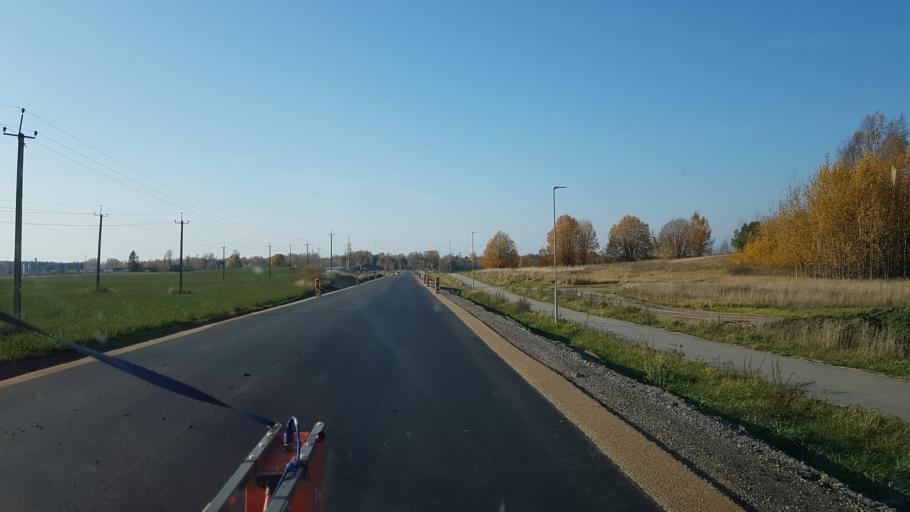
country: EE
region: Vorumaa
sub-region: Antsla vald
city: Vana-Antsla
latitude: 57.8382
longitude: 26.4957
